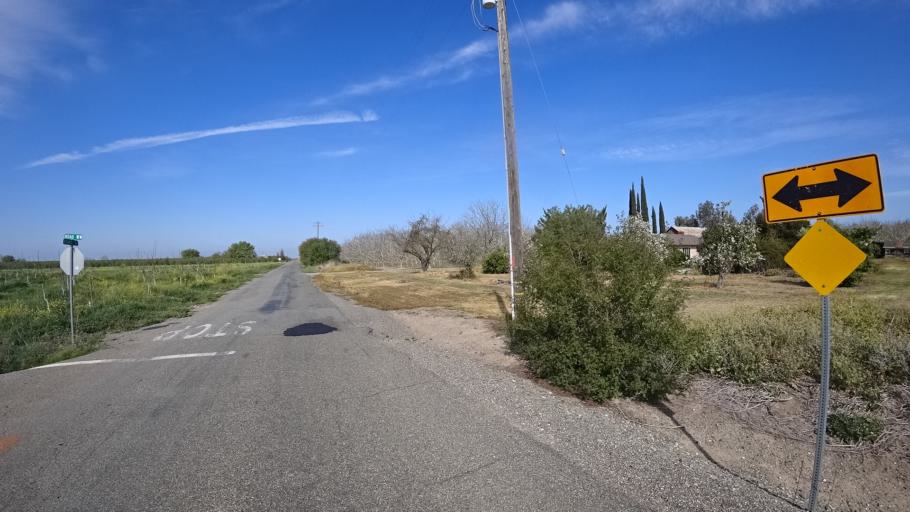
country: US
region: California
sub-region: Glenn County
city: Hamilton City
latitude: 39.6307
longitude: -122.0368
